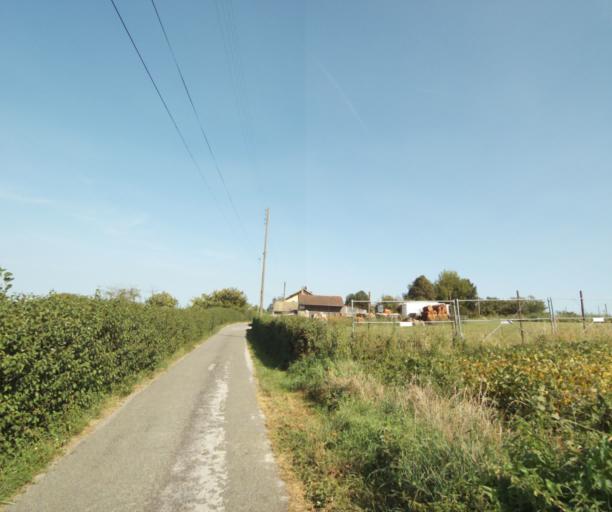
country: FR
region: Bourgogne
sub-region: Departement de Saone-et-Loire
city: Tournus
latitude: 46.5606
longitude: 4.8913
